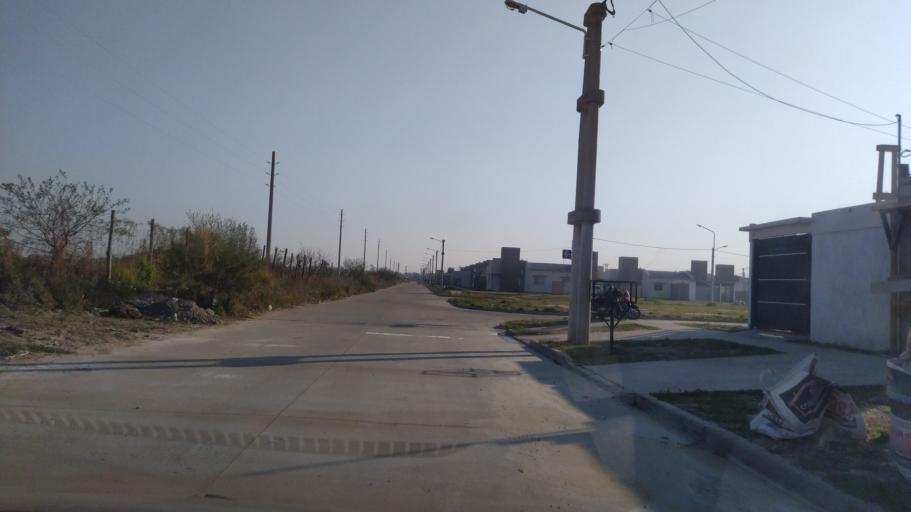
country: AR
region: Corrientes
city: Corrientes
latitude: -27.5275
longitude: -58.8083
